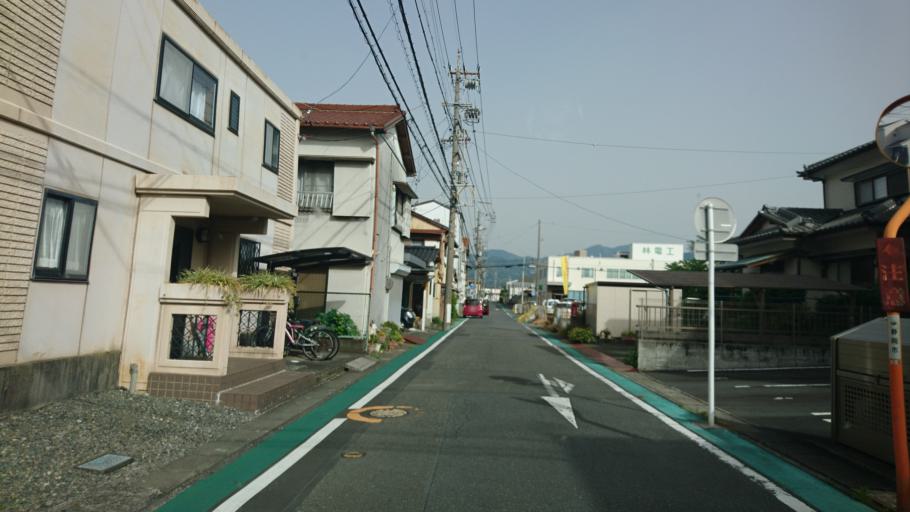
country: JP
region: Shizuoka
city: Shizuoka-shi
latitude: 35.0224
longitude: 138.4772
